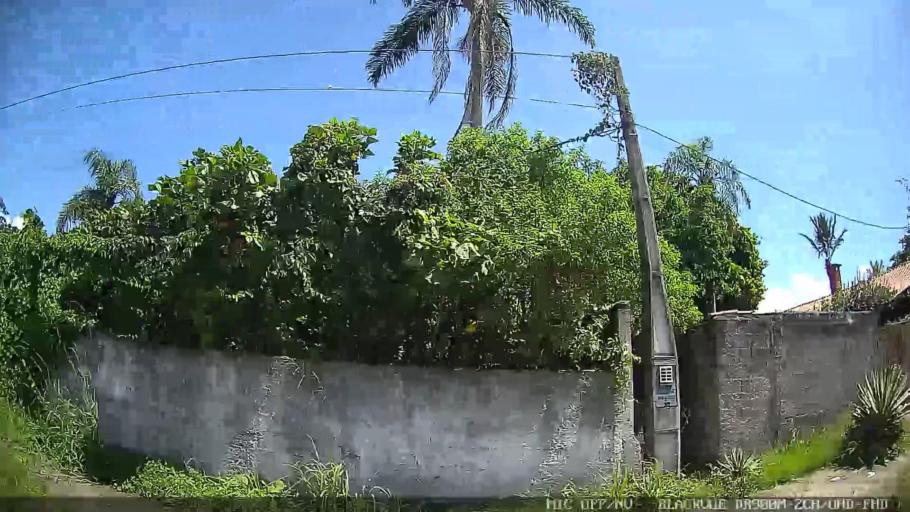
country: BR
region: Sao Paulo
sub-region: Caraguatatuba
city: Caraguatatuba
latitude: -23.6731
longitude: -45.4327
